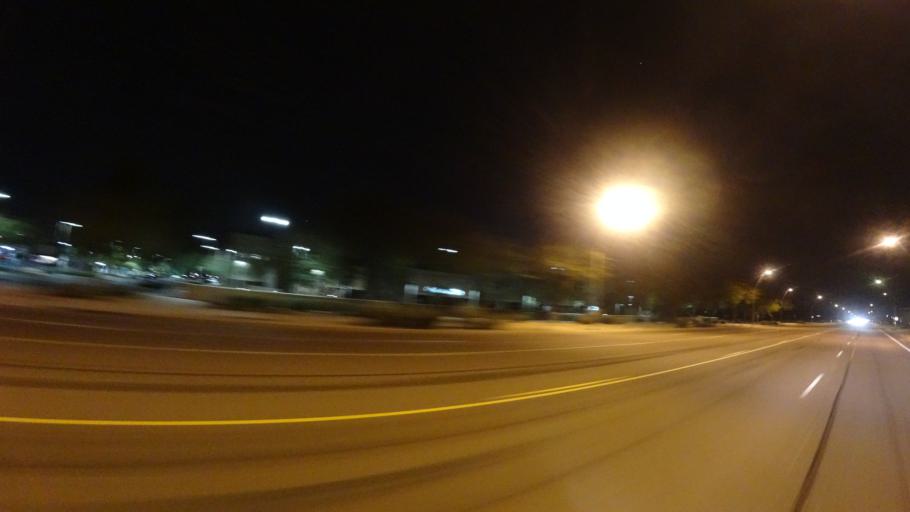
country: US
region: Arizona
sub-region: Maricopa County
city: Guadalupe
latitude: 33.3335
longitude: -111.9632
